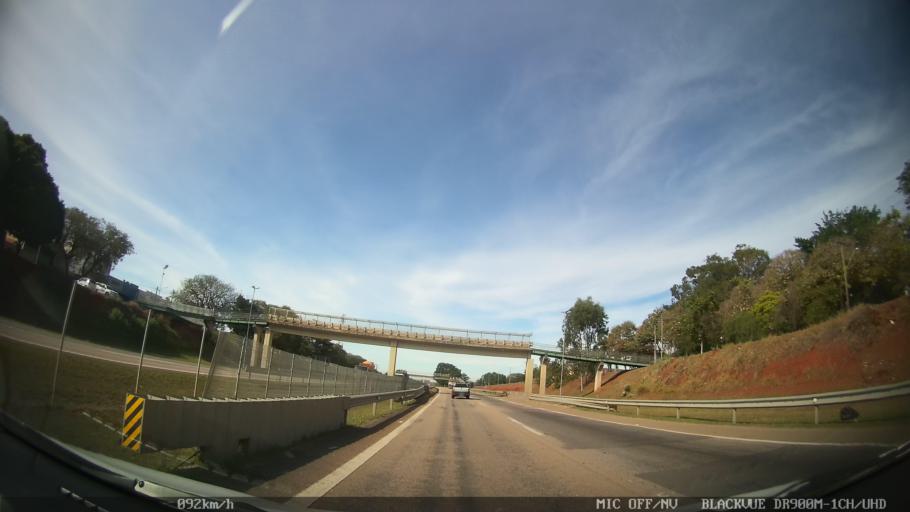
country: BR
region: Sao Paulo
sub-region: Rio Das Pedras
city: Rio das Pedras
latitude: -22.7720
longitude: -47.5932
